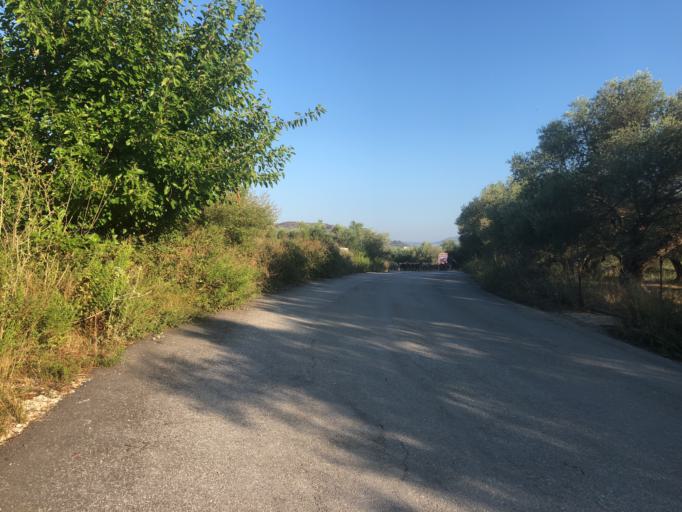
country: GR
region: Crete
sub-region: Nomos Chanias
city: Georgioupolis
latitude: 35.3381
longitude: 24.2861
